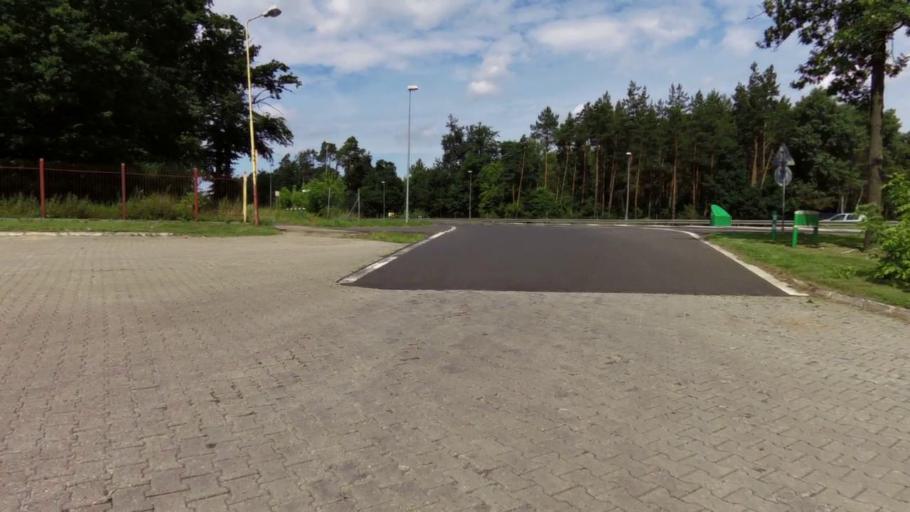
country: PL
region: West Pomeranian Voivodeship
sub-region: Powiat stargardzki
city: Kobylanka
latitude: 53.3485
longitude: 14.8380
